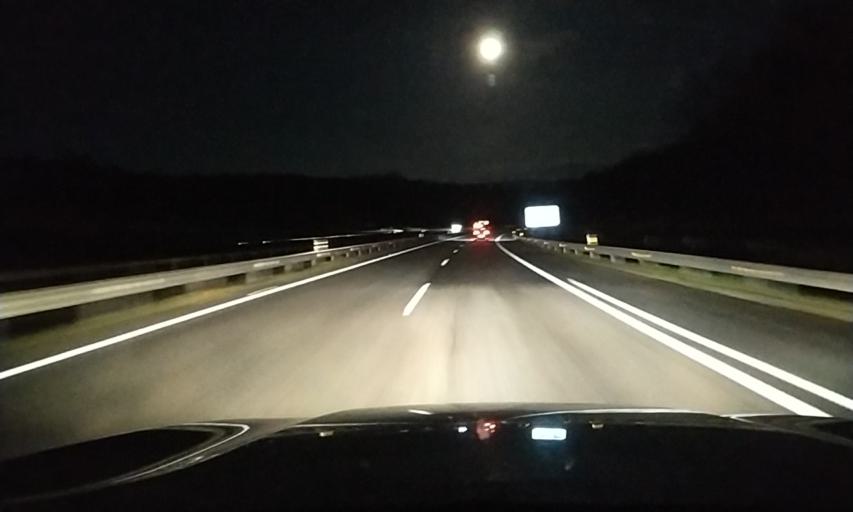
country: ES
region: Galicia
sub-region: Provincia de Ourense
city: Allariz
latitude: 42.2082
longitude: -7.8154
